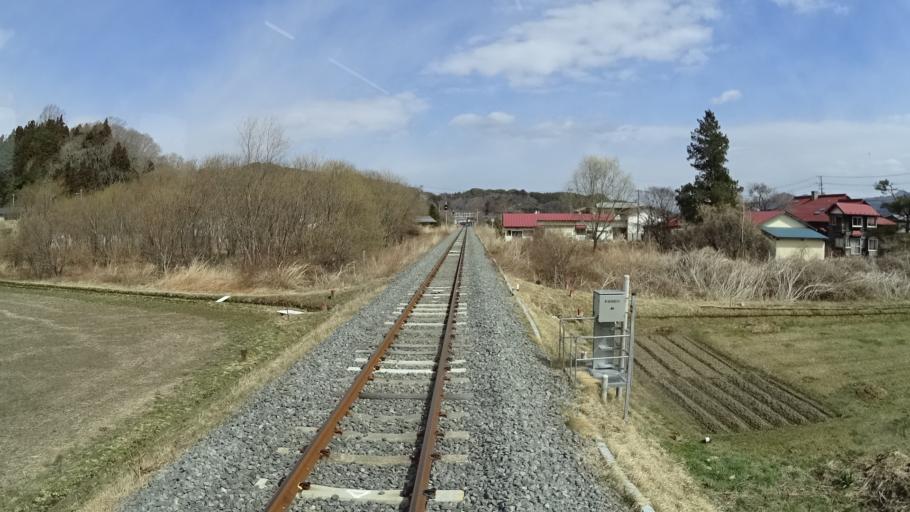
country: JP
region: Iwate
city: Miyako
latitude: 39.5751
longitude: 141.9341
